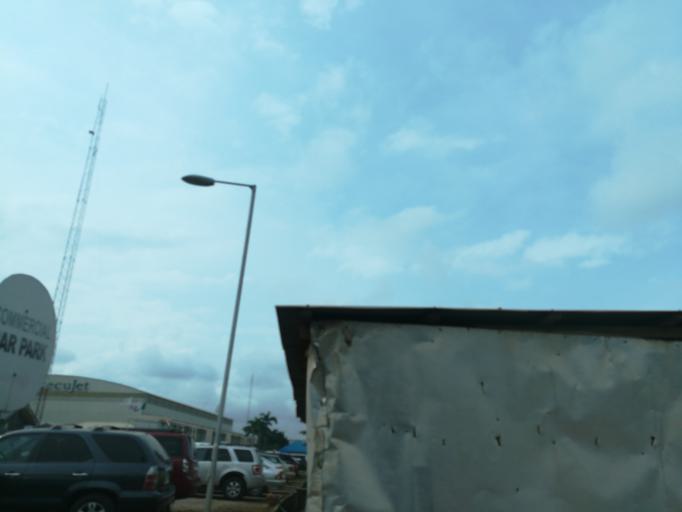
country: NG
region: Lagos
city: Oshodi
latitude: 6.5758
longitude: 3.3250
